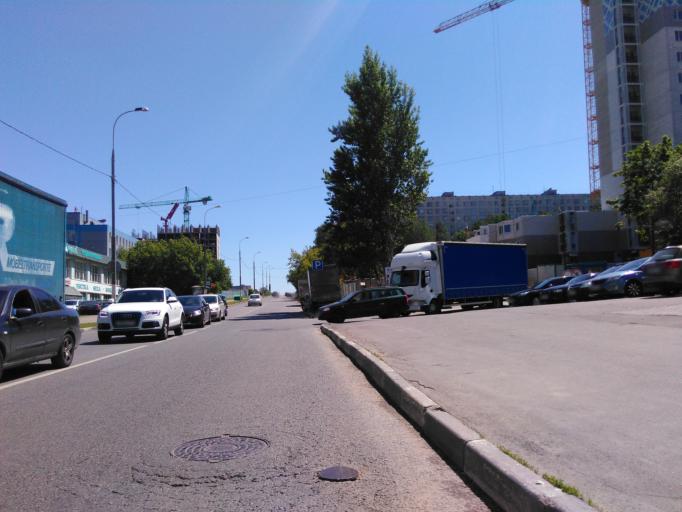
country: RU
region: Moskovskaya
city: Cheremushki
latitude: 55.6522
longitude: 37.5285
